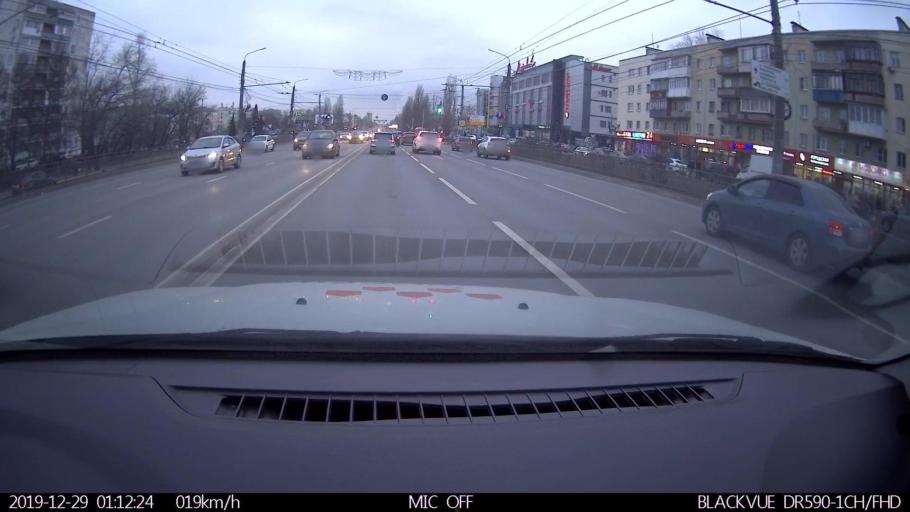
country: RU
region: Nizjnij Novgorod
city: Nizhniy Novgorod
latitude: 56.2834
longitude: 43.9314
